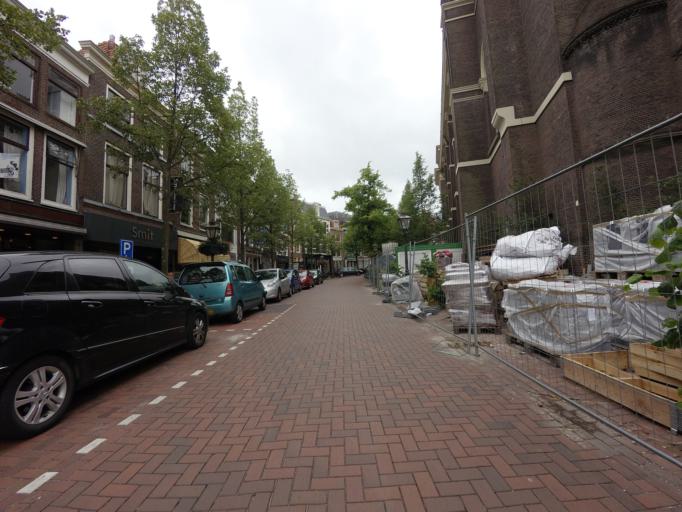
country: NL
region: South Holland
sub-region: Gemeente Leiden
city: Leiden
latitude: 52.1610
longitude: 4.4908
